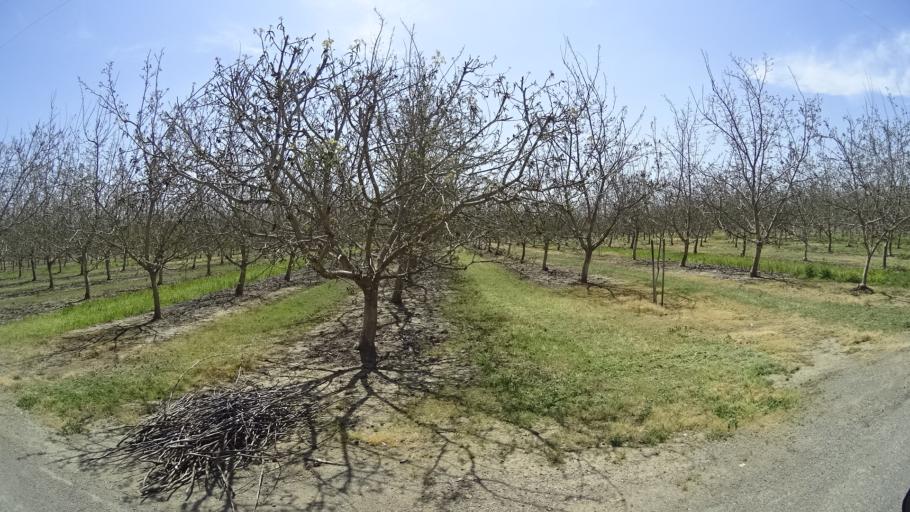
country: US
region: California
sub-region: Glenn County
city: Willows
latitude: 39.5110
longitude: -122.0151
